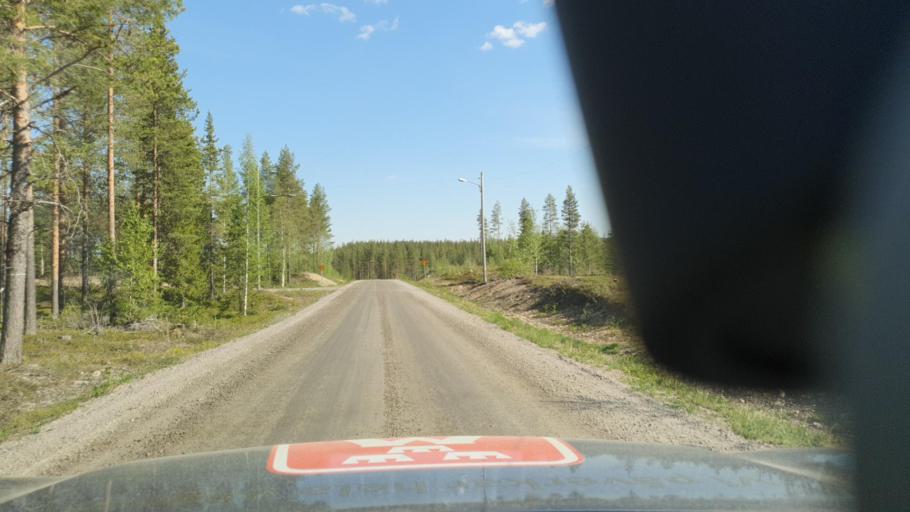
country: SE
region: Norrbotten
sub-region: Bodens Kommun
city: Boden
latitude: 66.5173
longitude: 21.9064
